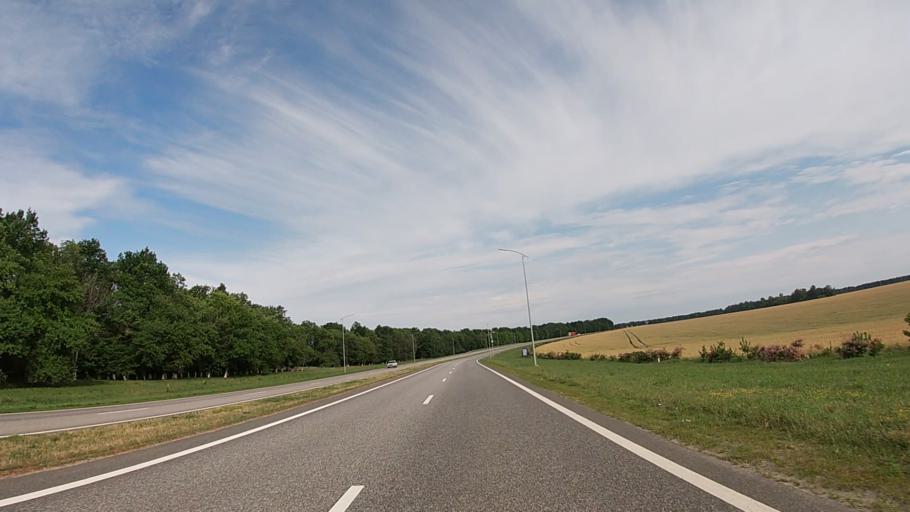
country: RU
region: Belgorod
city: Borisovka
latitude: 50.7534
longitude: 35.9692
